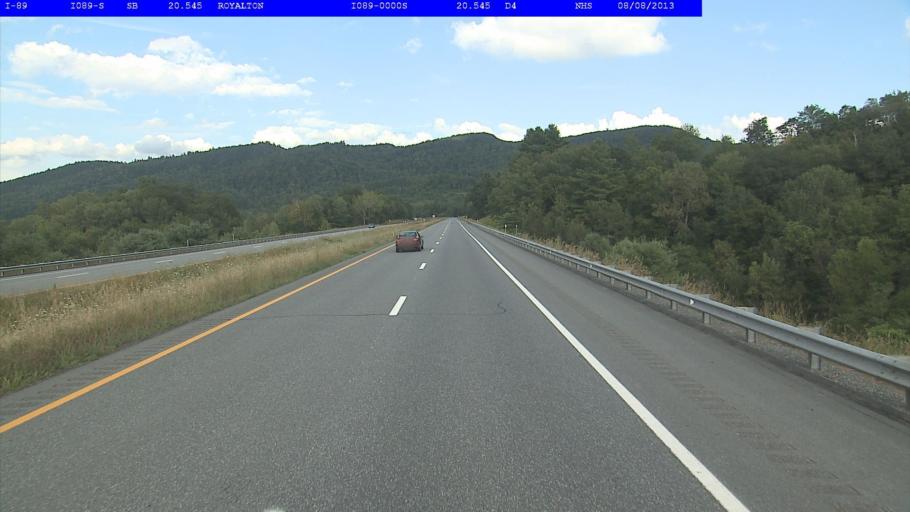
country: US
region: Vermont
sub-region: Orange County
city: Randolph
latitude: 43.8113
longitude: -72.5577
